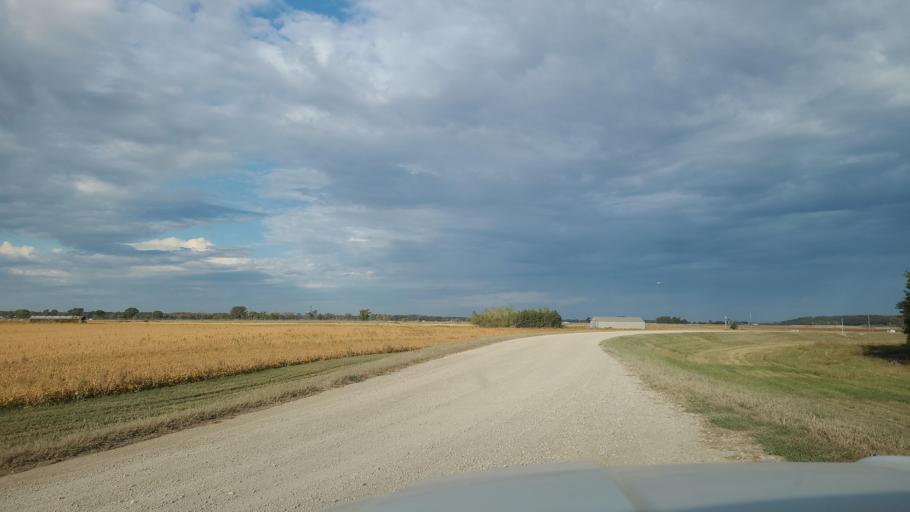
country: US
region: Kansas
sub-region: Douglas County
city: Lawrence
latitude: 39.0127
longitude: -95.2057
